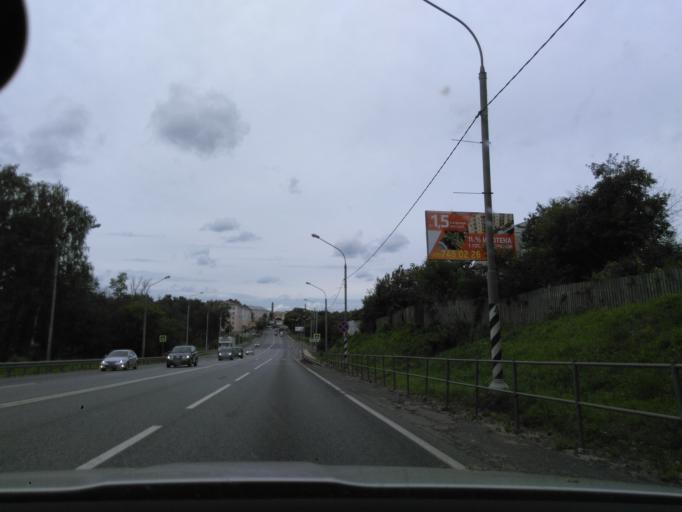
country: RU
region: Moskovskaya
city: Klin
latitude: 56.3288
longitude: 36.7402
